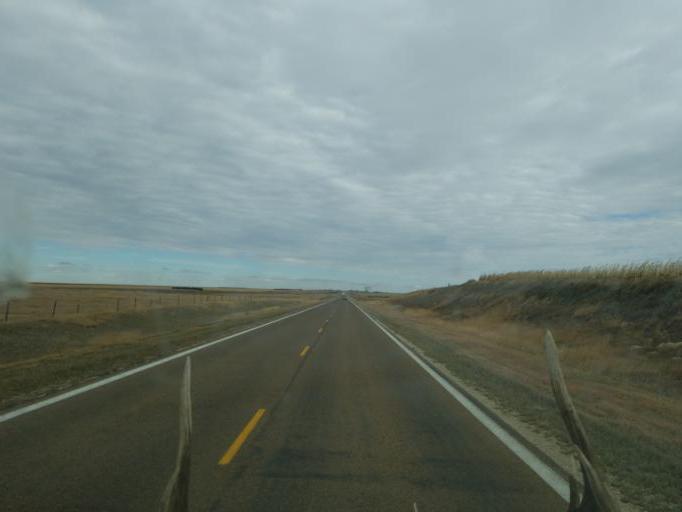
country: US
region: Kansas
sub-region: Logan County
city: Oakley
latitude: 39.0768
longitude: -101.1972
